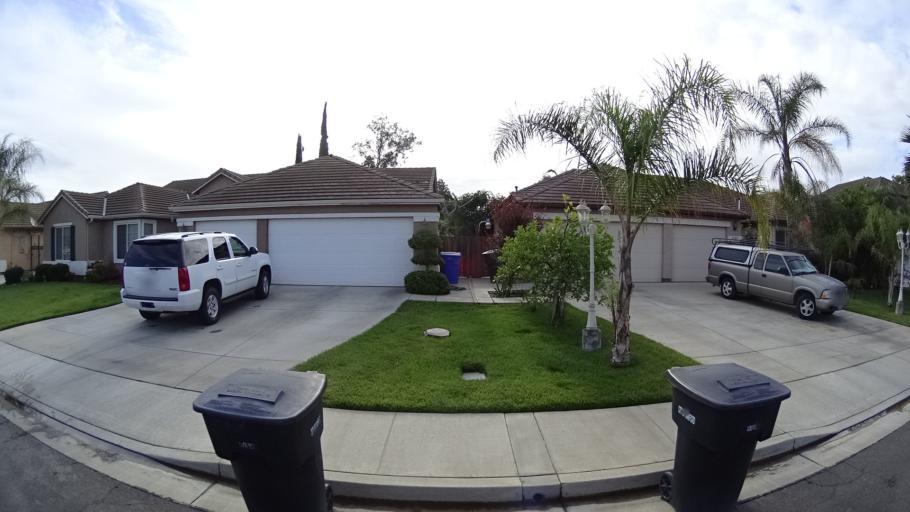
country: US
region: California
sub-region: Kings County
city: Hanford
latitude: 36.3435
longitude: -119.6758
